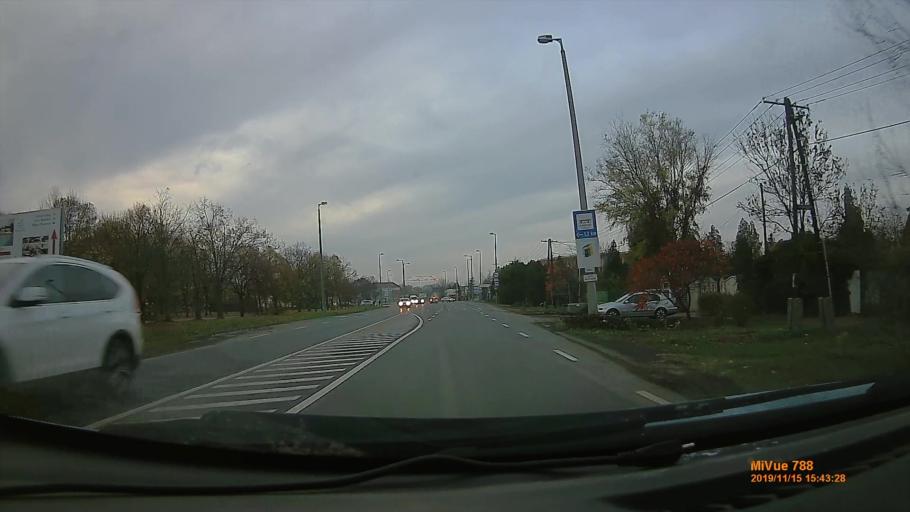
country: HU
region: Bekes
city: Bekescsaba
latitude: 46.6808
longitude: 21.1161
